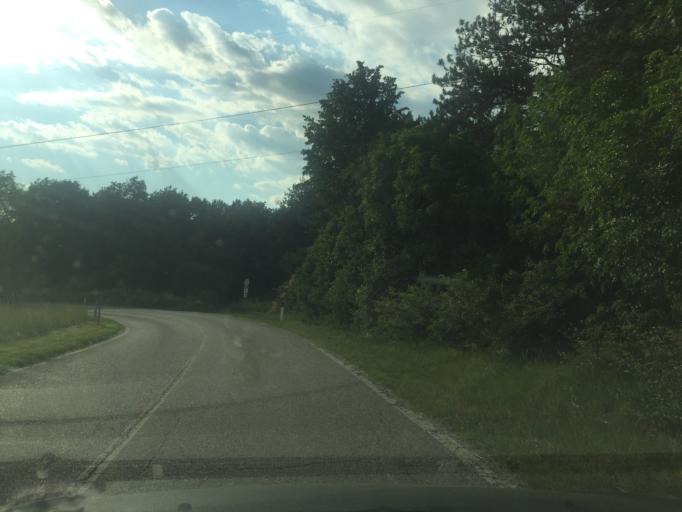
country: IT
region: Friuli Venezia Giulia
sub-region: Provincia di Gorizia
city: Gradisca d'Isonzo
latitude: 45.8721
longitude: 13.5119
